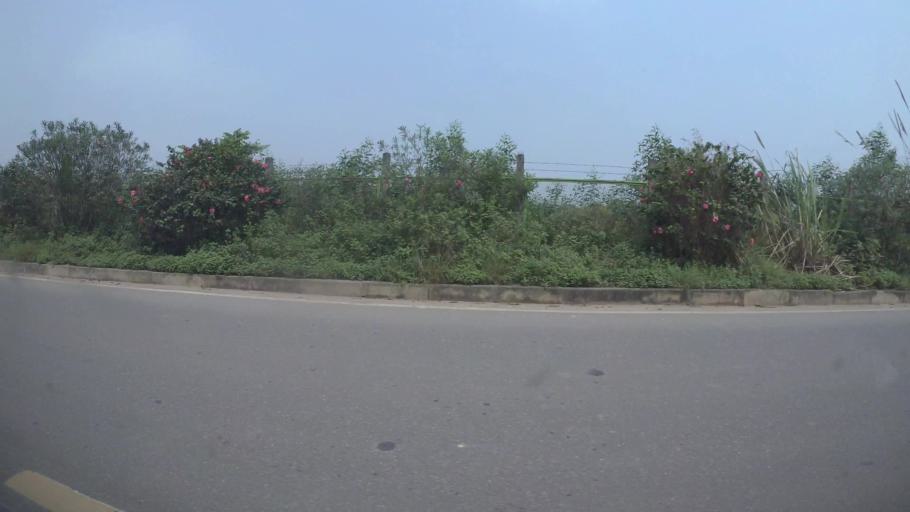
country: VN
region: Ha Noi
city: Quoc Oai
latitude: 20.9990
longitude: 105.5988
